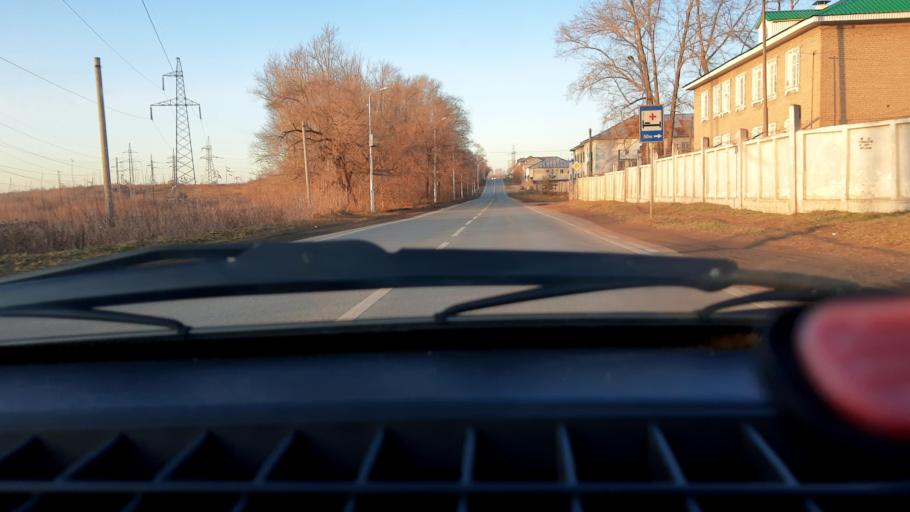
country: RU
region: Bashkortostan
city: Blagoveshchensk
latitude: 54.8964
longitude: 56.0545
